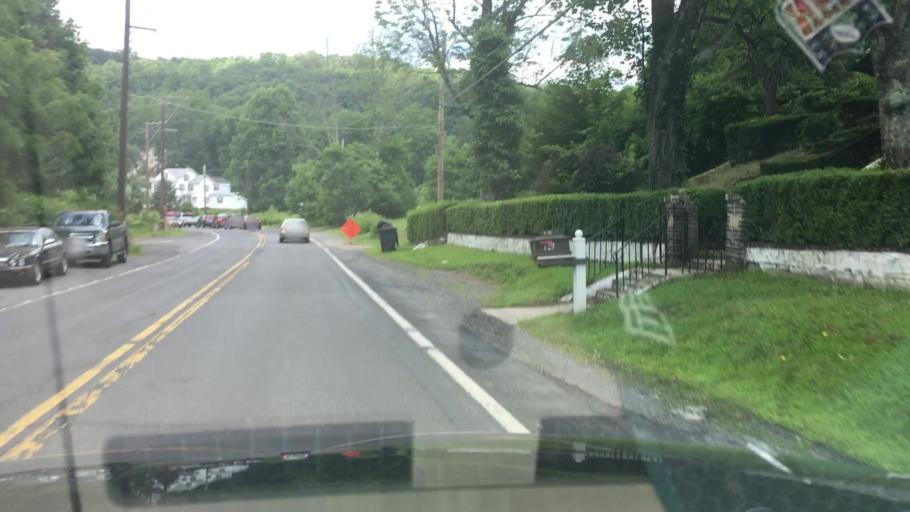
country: US
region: Pennsylvania
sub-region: Schuylkill County
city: Minersville
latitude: 40.6983
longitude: -76.2847
